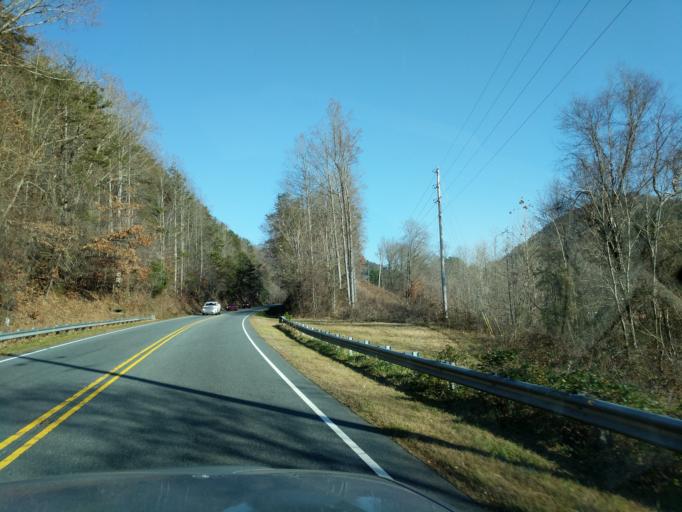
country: US
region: North Carolina
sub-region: McDowell County
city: West Marion
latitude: 35.5201
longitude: -81.9738
